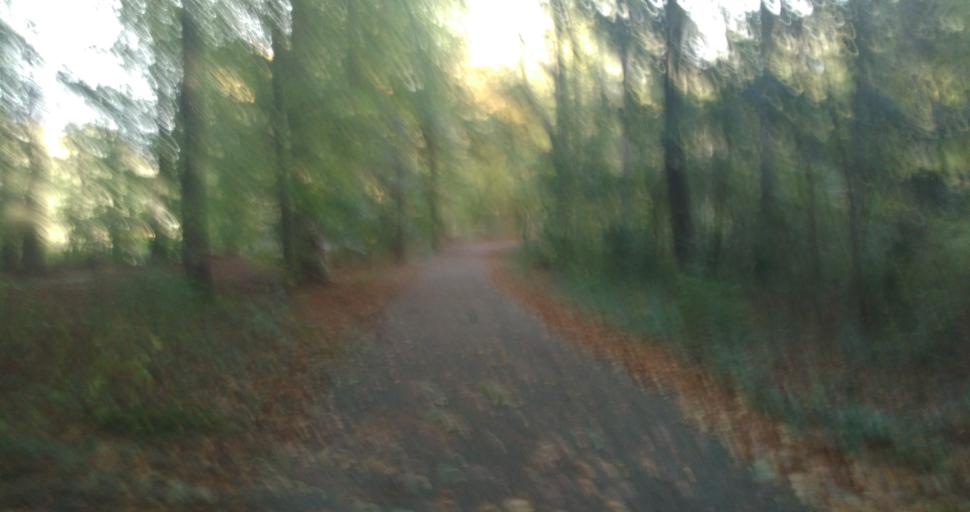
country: NL
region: North Holland
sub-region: Gemeente Amstelveen
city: Amstelveen
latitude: 52.3167
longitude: 4.8316
